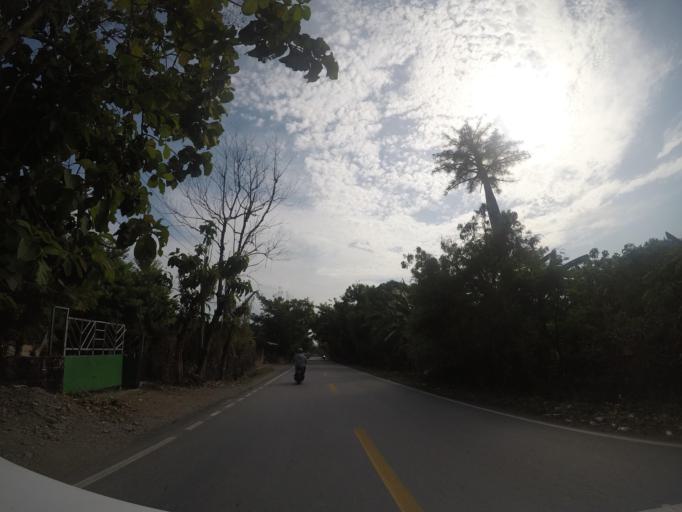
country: ID
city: Metinaro
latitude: -8.5496
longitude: 125.6643
